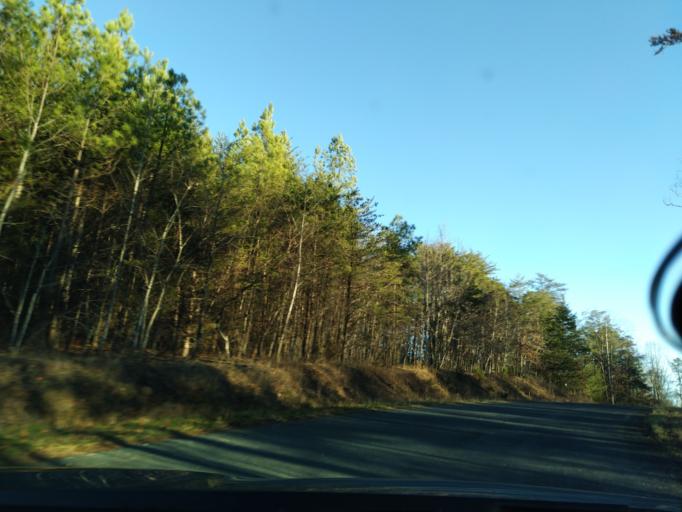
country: US
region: Virginia
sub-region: Appomattox County
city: Appomattox
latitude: 37.3825
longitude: -78.6421
